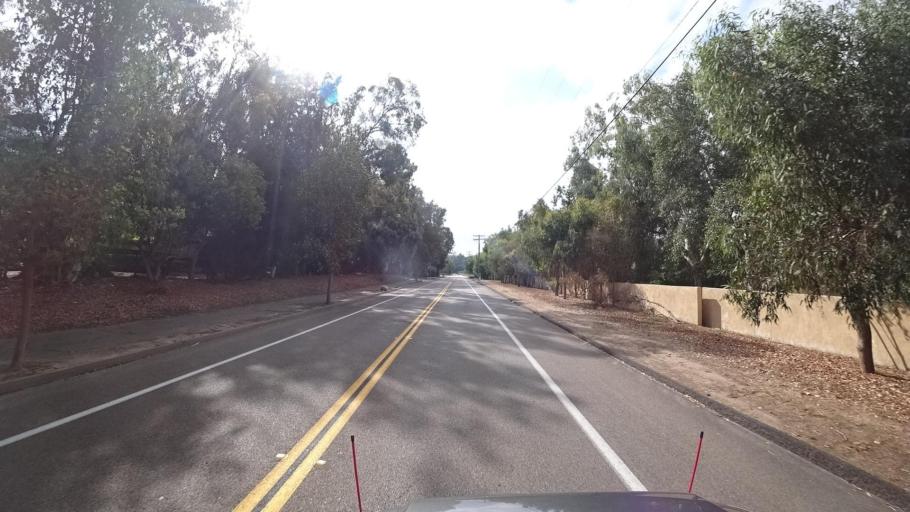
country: US
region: California
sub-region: San Diego County
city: Rancho Santa Fe
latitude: 33.0060
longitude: -117.2368
